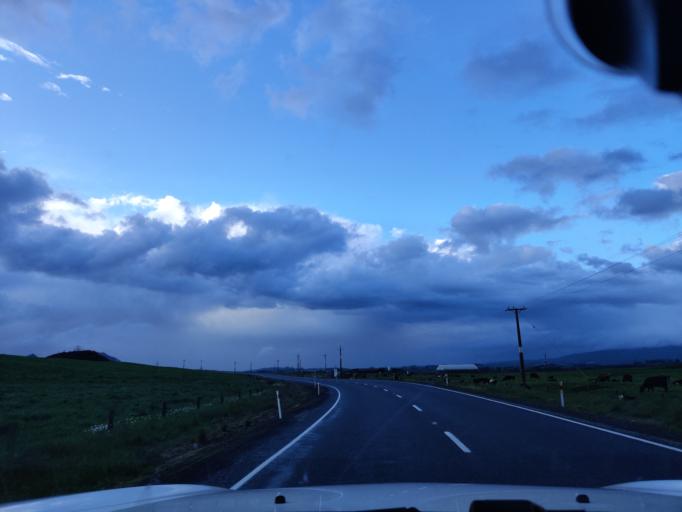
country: NZ
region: Waikato
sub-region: South Waikato District
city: Tokoroa
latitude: -38.3904
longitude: 175.7807
